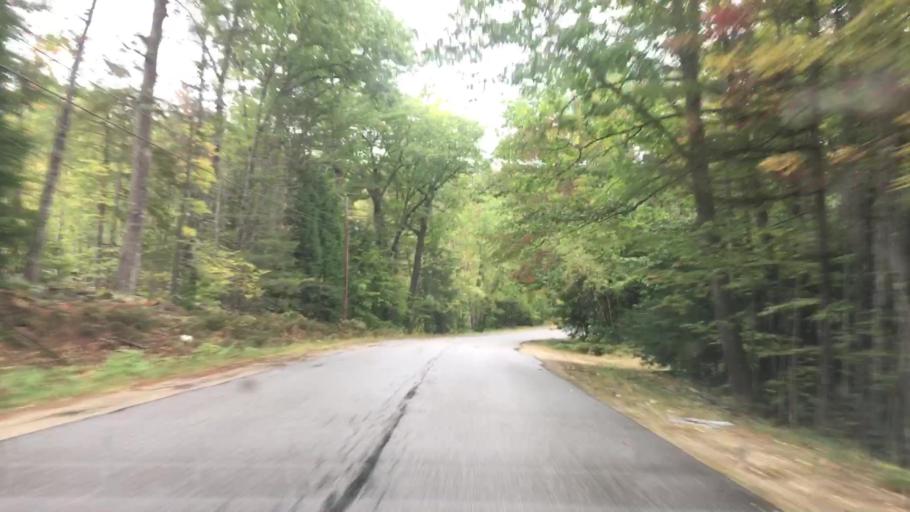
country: US
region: Maine
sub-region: Cumberland County
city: Harrison
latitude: 44.0514
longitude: -70.6178
